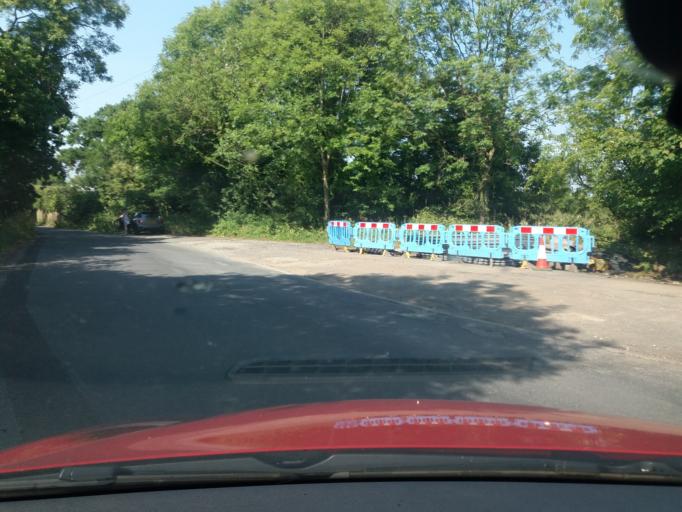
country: GB
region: England
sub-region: Lancashire
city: Euxton
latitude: 53.6699
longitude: -2.6671
